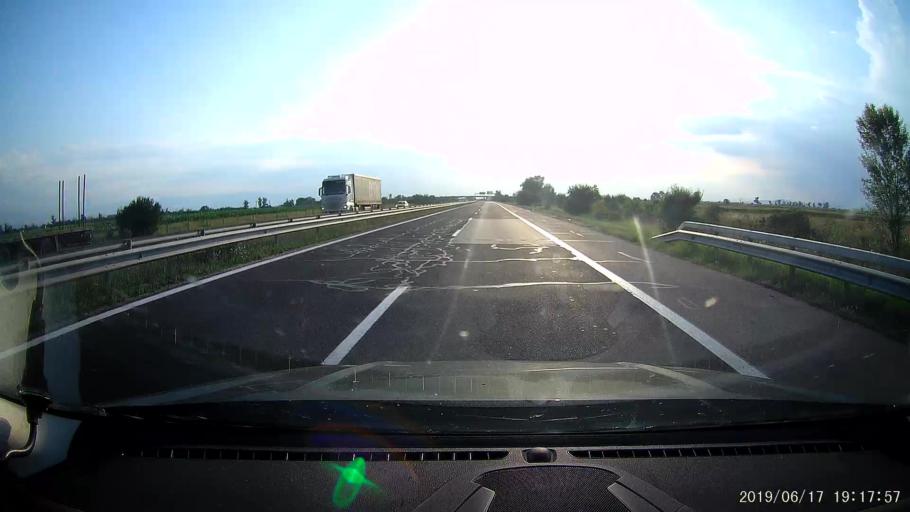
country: BG
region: Plovdiv
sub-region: Obshtina Suedinenie
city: Suedinenie
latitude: 42.2038
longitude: 24.5743
